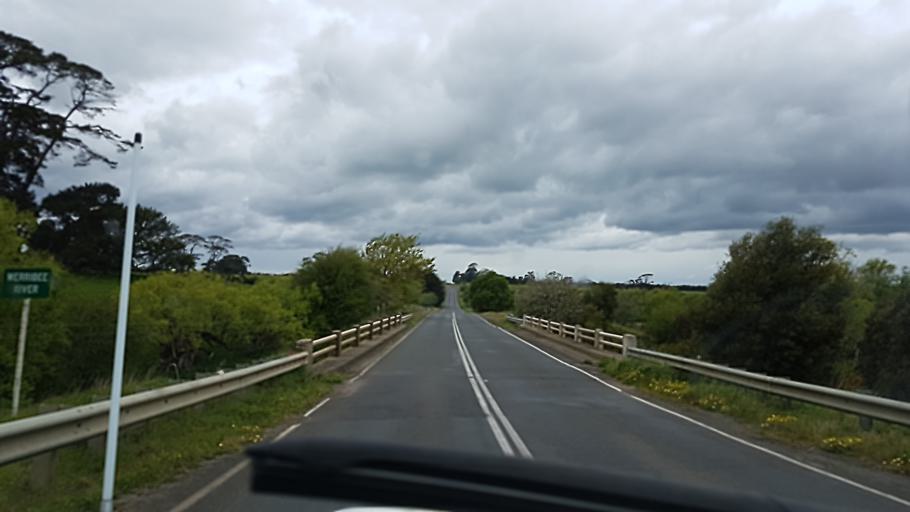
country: AU
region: Victoria
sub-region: Moorabool
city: Bacchus Marsh
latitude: -37.6004
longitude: 144.2495
